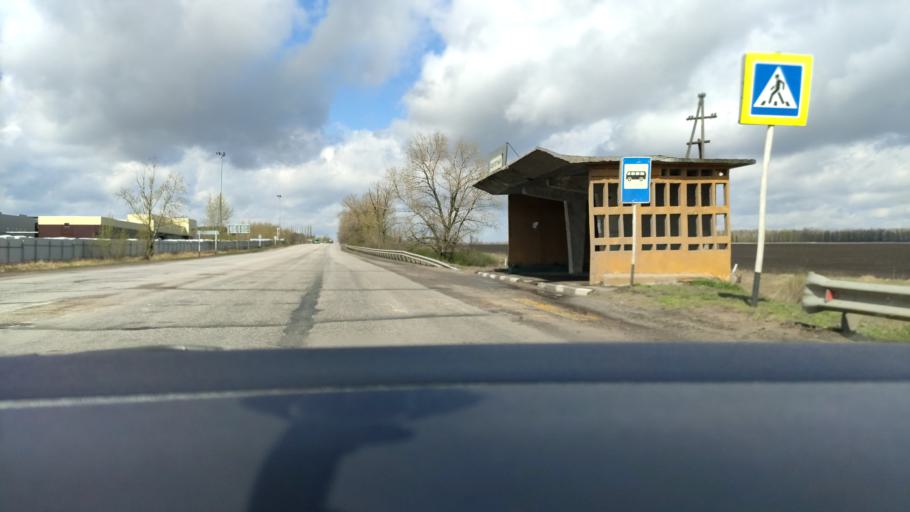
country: RU
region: Voronezj
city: Maslovka
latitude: 51.5520
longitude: 39.2809
